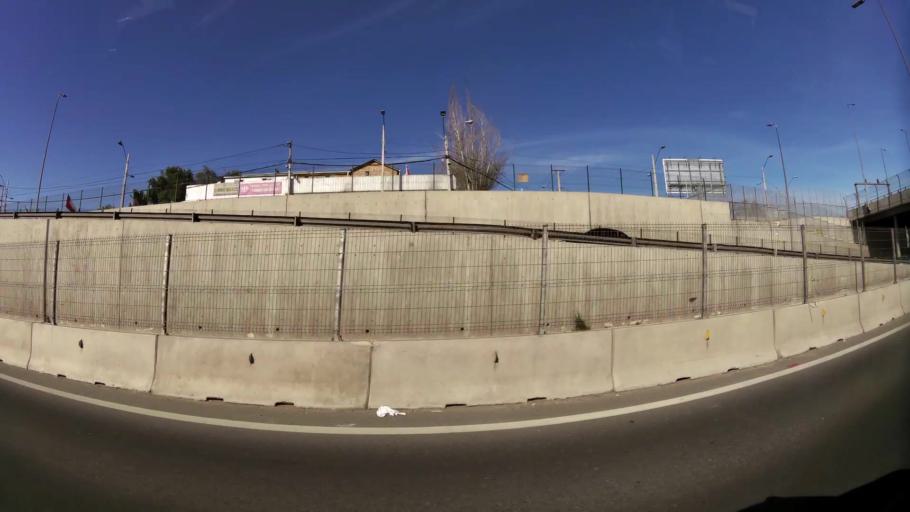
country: CL
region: Santiago Metropolitan
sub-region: Provincia de Santiago
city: La Pintana
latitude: -33.5412
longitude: -70.6205
